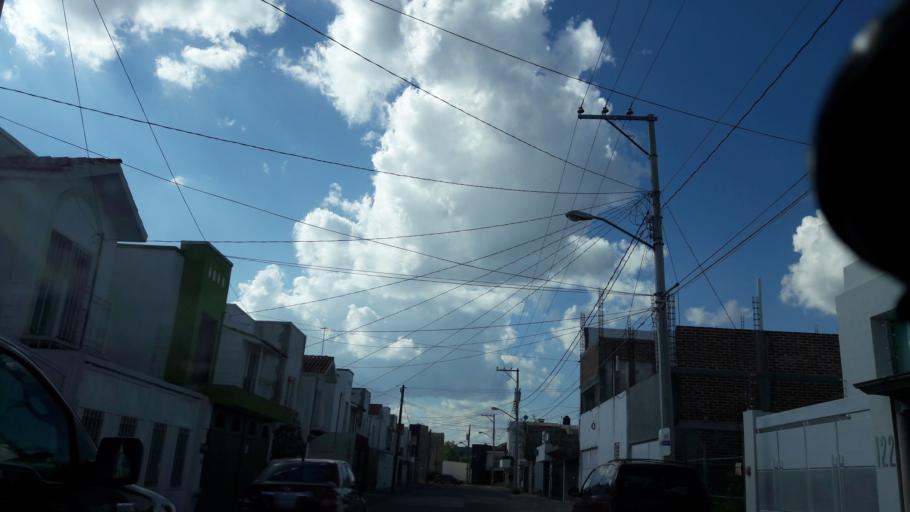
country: MX
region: Guanajuato
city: Leon
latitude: 21.1749
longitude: -101.6689
